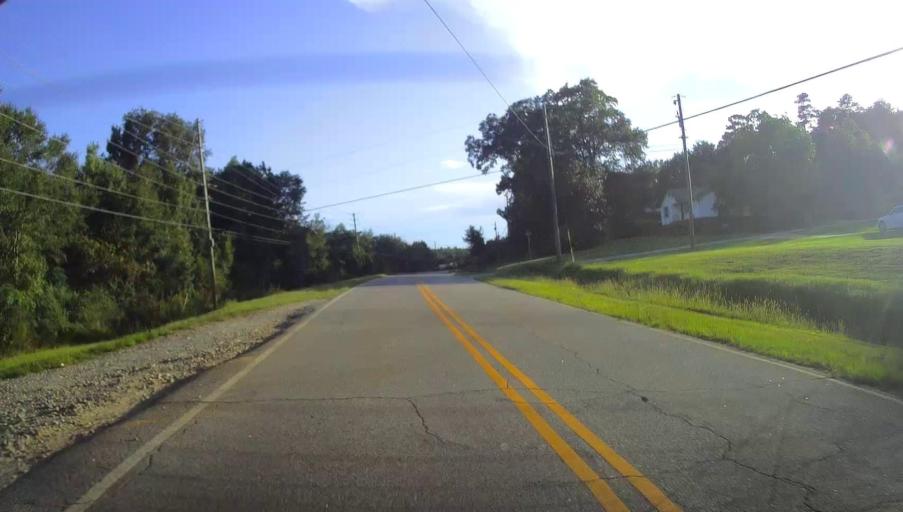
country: US
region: Georgia
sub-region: Muscogee County
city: Columbus
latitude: 32.4278
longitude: -85.0145
